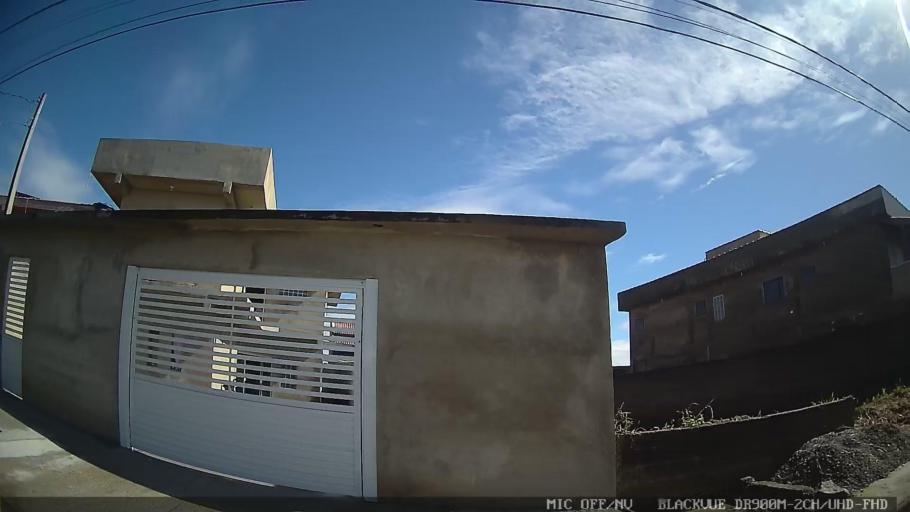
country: BR
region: Sao Paulo
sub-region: Itanhaem
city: Itanhaem
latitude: -24.2405
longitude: -46.8833
